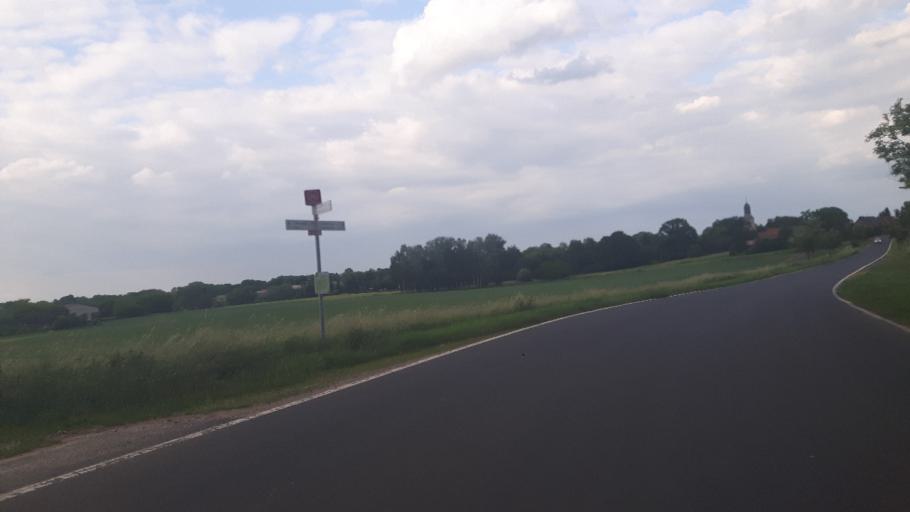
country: DE
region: Brandenburg
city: Hohenfinow
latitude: 52.8091
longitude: 13.9172
